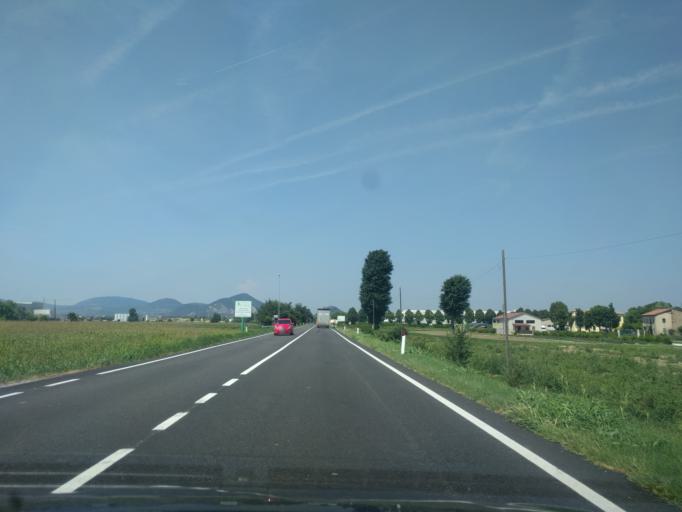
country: IT
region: Veneto
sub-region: Provincia di Padova
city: Solesino
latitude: 45.1981
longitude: 11.7557
